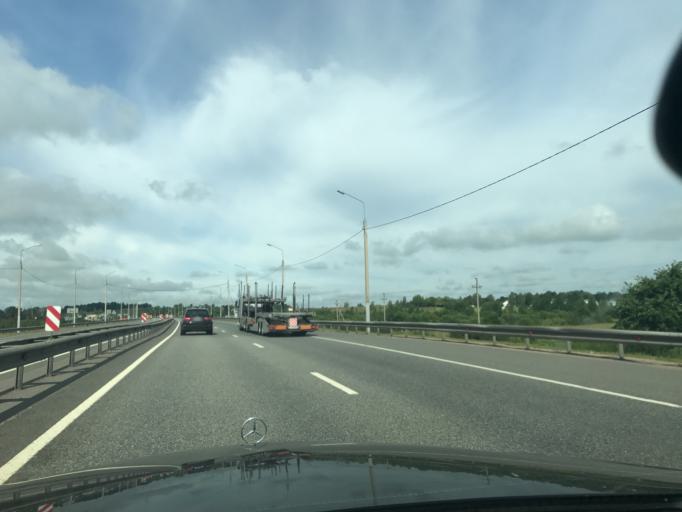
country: RU
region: Smolensk
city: Yartsevo
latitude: 55.0791
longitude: 32.6867
